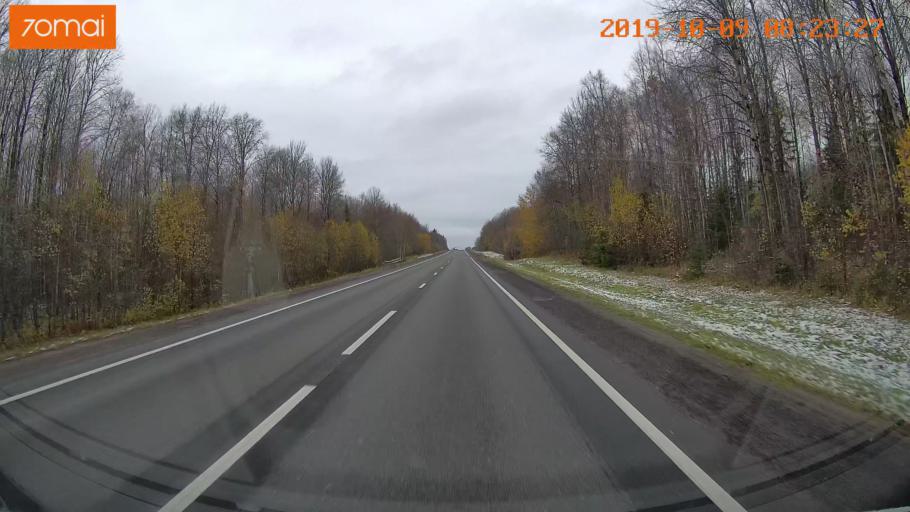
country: RU
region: Vologda
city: Gryazovets
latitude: 58.7546
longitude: 40.2833
